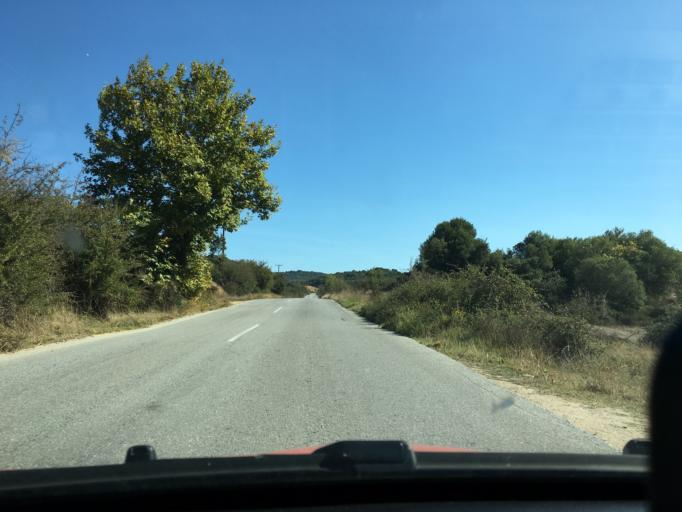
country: GR
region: Central Macedonia
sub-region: Nomos Chalkidikis
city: Megali Panagia
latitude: 40.3854
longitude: 23.7114
